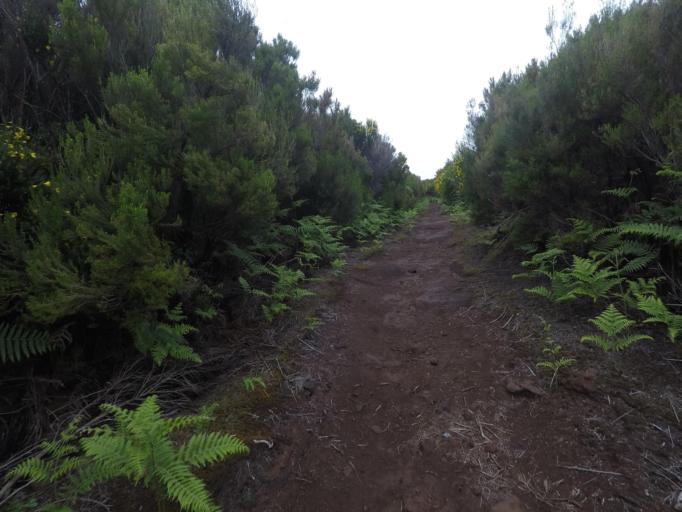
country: PT
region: Madeira
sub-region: Calheta
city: Arco da Calheta
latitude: 32.7771
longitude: -17.1327
